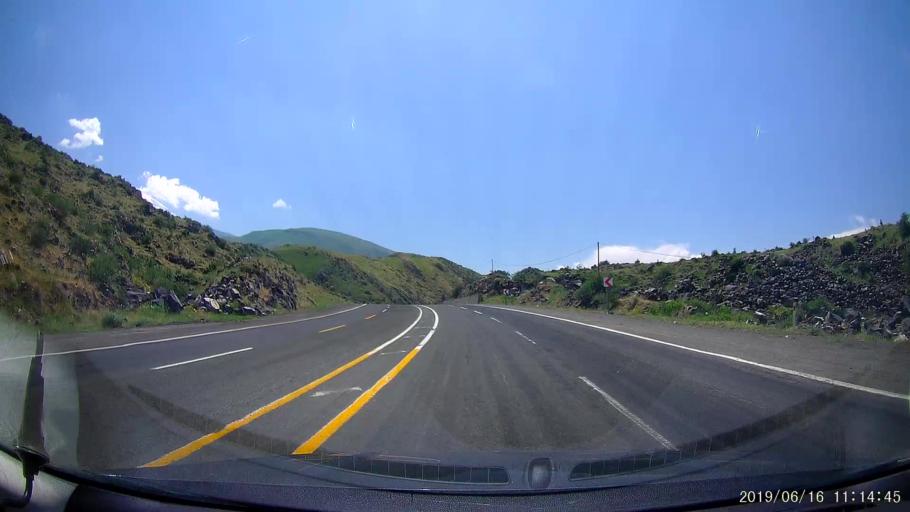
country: TR
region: Igdir
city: Igdir
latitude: 39.7737
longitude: 44.1415
